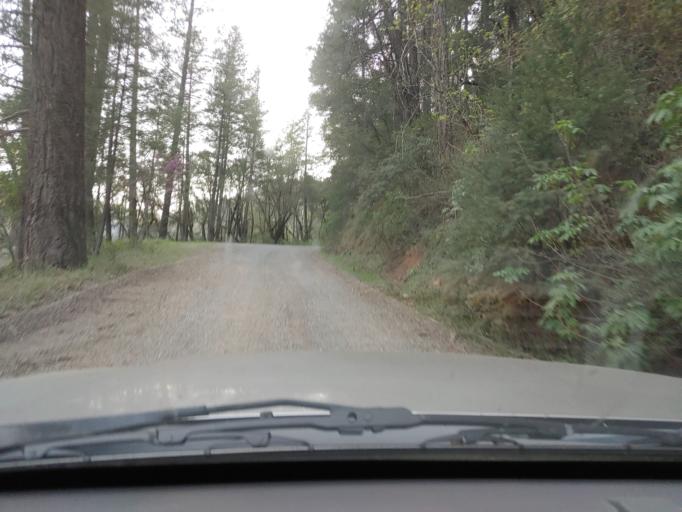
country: US
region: California
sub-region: Shasta County
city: Bella Vista
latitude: 40.8391
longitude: -122.0204
